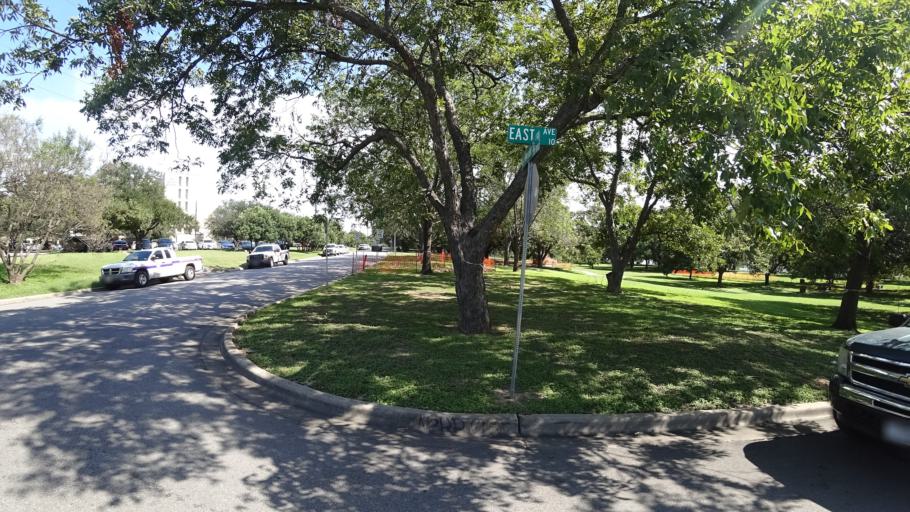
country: US
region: Texas
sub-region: Travis County
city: Austin
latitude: 30.2522
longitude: -97.7349
